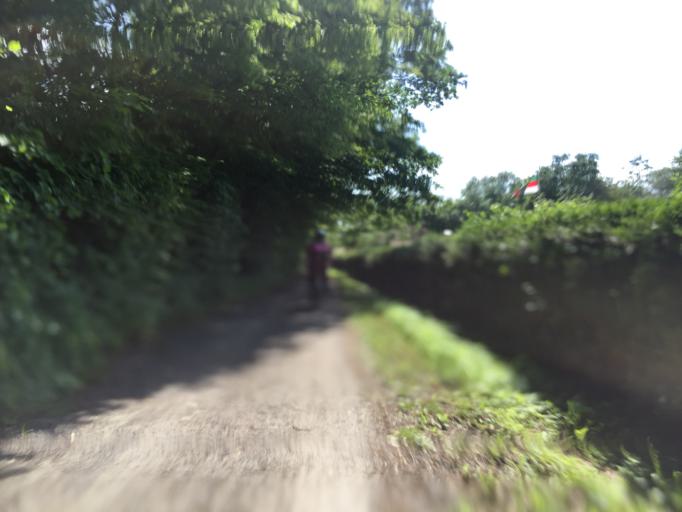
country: DE
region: Bavaria
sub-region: Regierungsbezirk Unterfranken
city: Aschaffenburg
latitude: 49.9798
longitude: 9.1623
